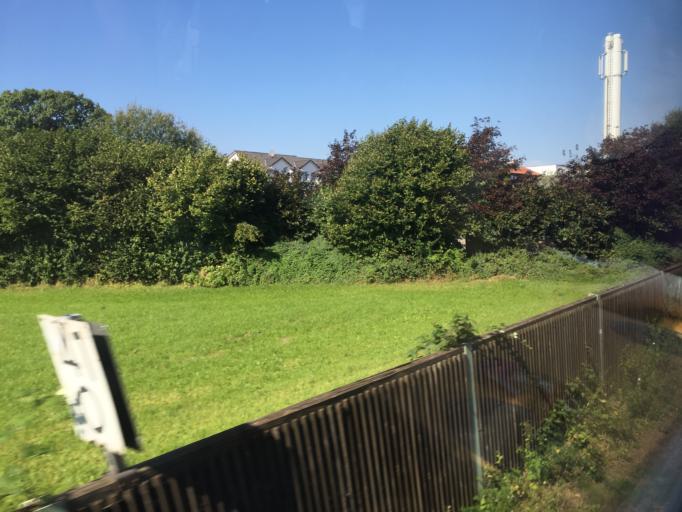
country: DE
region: Schleswig-Holstein
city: Delingsdorf
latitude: 53.6804
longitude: 10.2483
